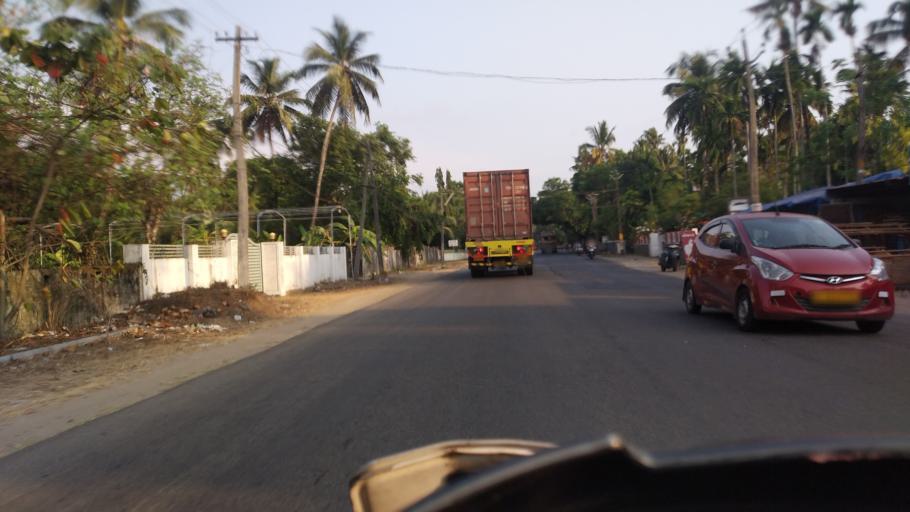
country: IN
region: Kerala
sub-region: Thrissur District
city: Thanniyam
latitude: 10.3933
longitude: 76.1173
